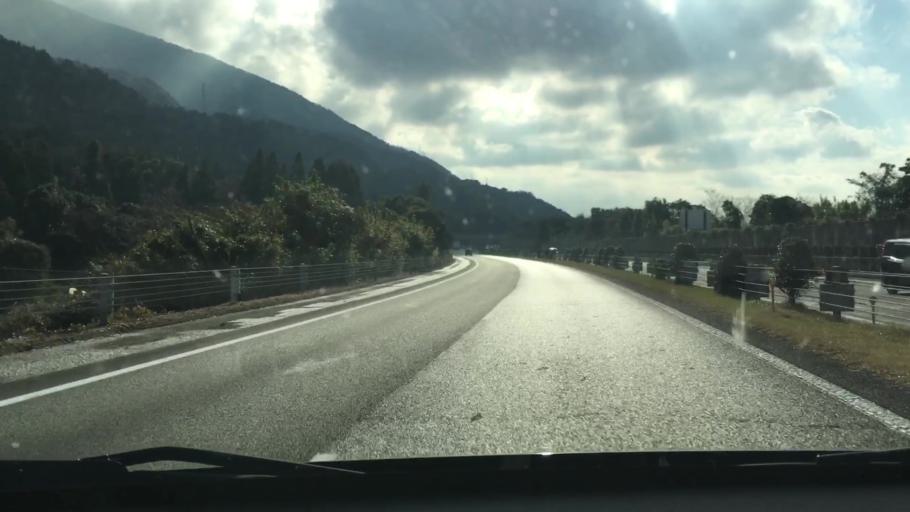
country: JP
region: Kumamoto
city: Yatsushiro
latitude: 32.5370
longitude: 130.6732
